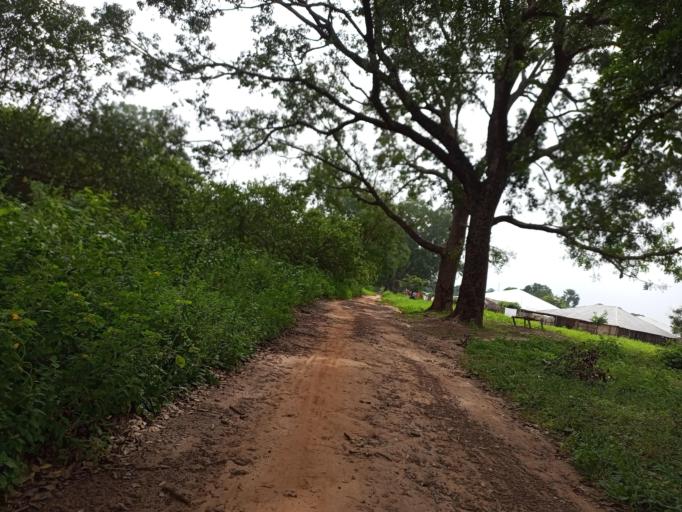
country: GW
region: Oio
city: Farim
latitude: 12.4361
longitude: -15.4210
